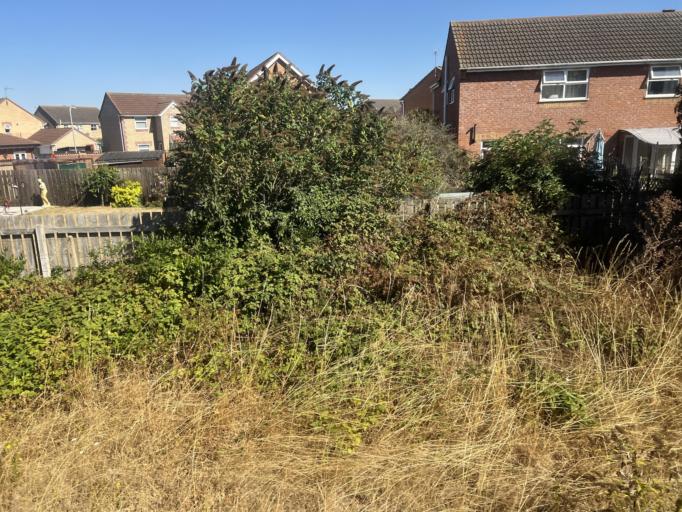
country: GB
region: England
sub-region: Lincolnshire
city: Sleaford
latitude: 52.9940
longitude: -0.3927
